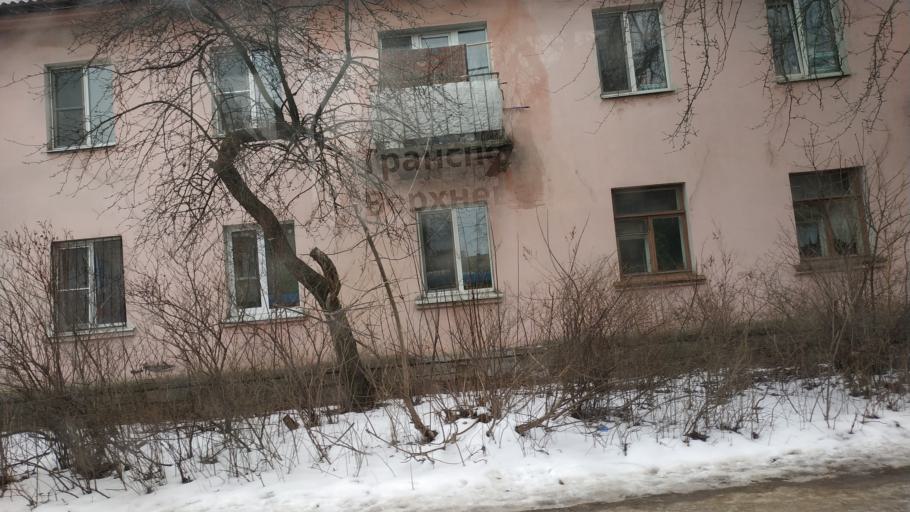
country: RU
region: Tverskaya
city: Tver
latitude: 56.8773
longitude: 35.9047
